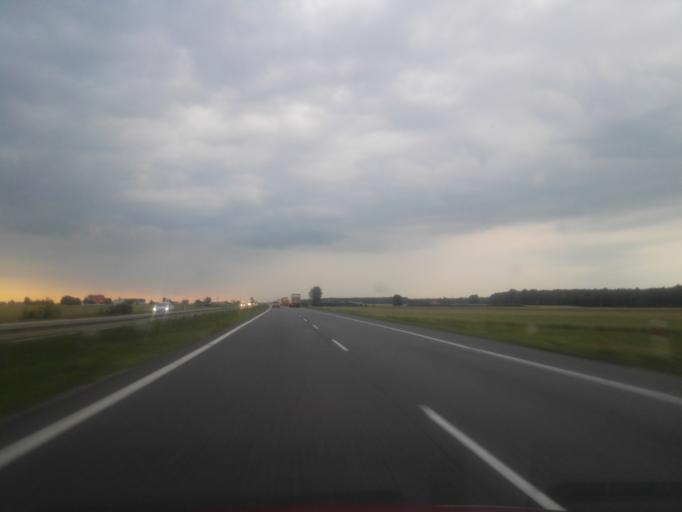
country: PL
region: Lodz Voivodeship
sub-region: Powiat piotrkowski
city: Wola Krzysztoporska
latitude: 51.3767
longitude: 19.6215
